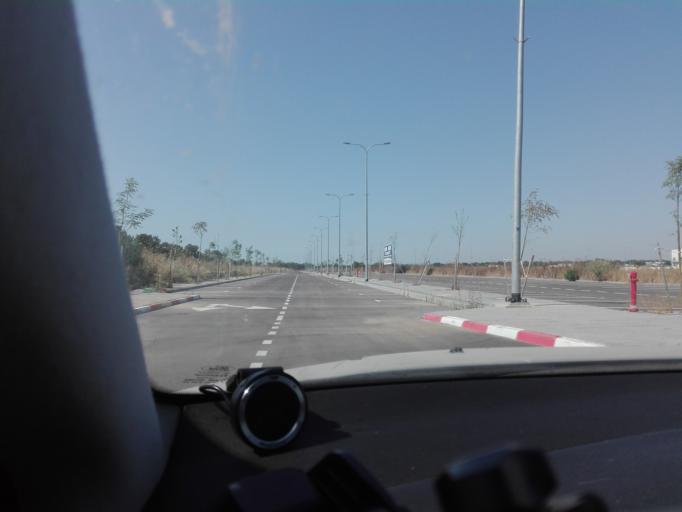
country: IL
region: Central District
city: Bene 'Ayish
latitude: 31.7240
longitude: 34.7558
